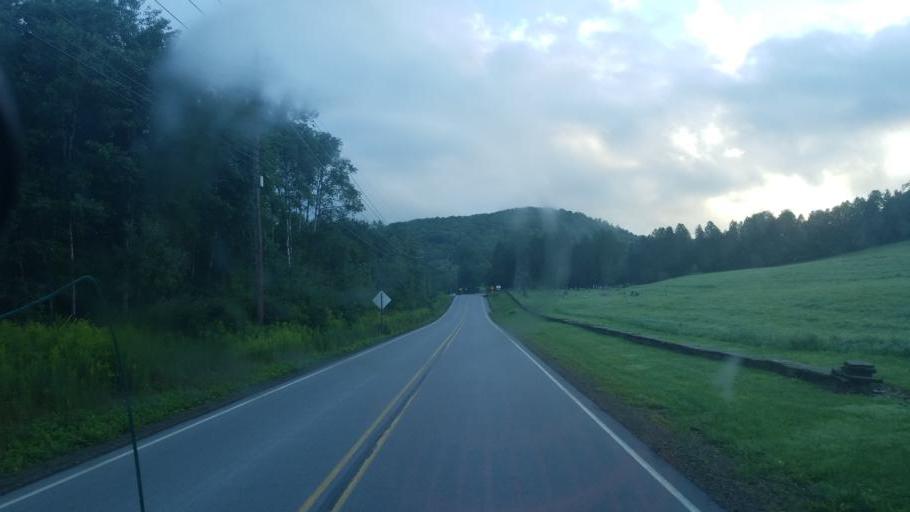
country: US
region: Pennsylvania
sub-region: Potter County
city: Galeton
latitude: 41.8340
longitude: -77.7961
